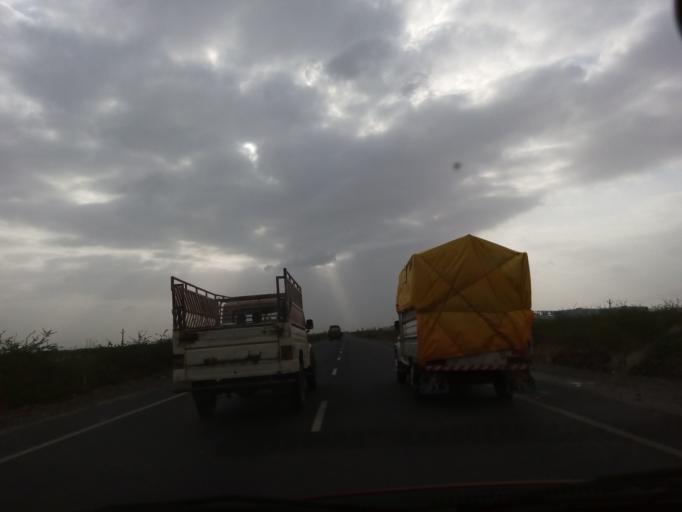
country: IN
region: Gujarat
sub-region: Kachchh
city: Bhuj
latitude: 23.2477
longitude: 69.8460
